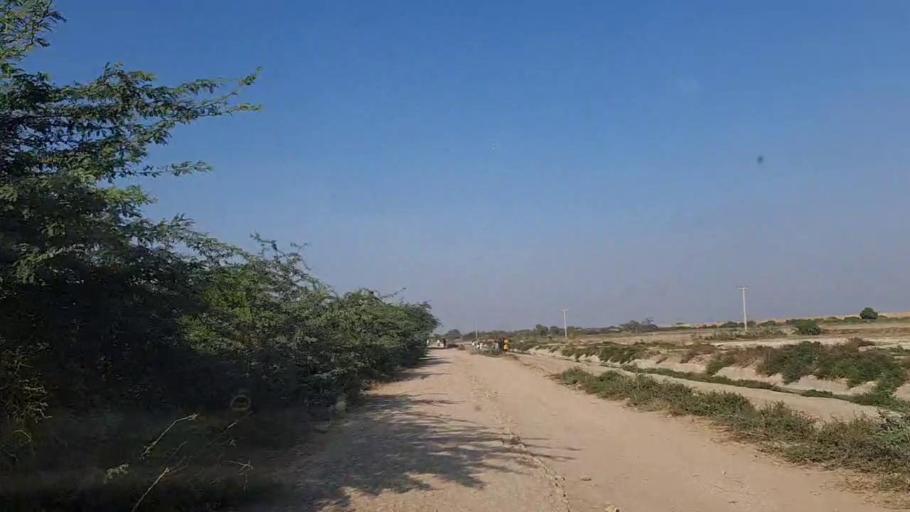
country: PK
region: Sindh
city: Thatta
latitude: 24.7404
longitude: 67.9675
